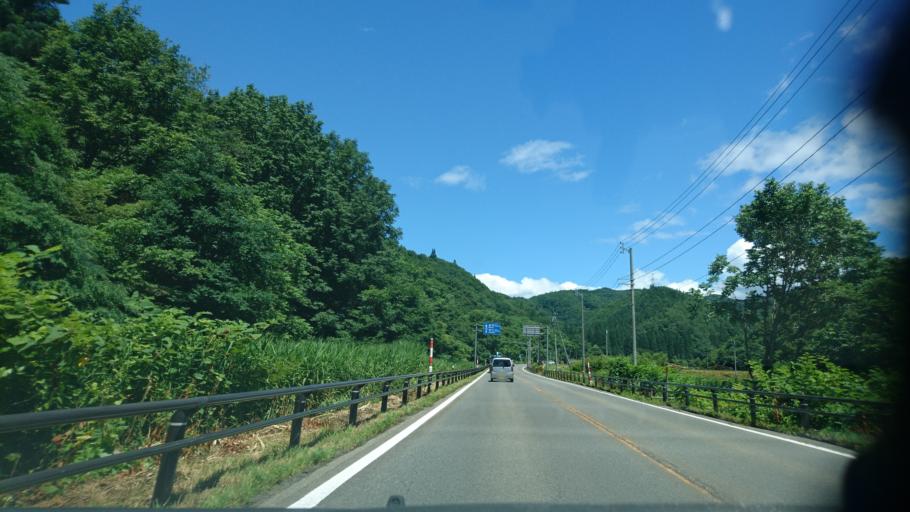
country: JP
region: Akita
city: Kakunodatemachi
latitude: 39.6560
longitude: 140.6723
